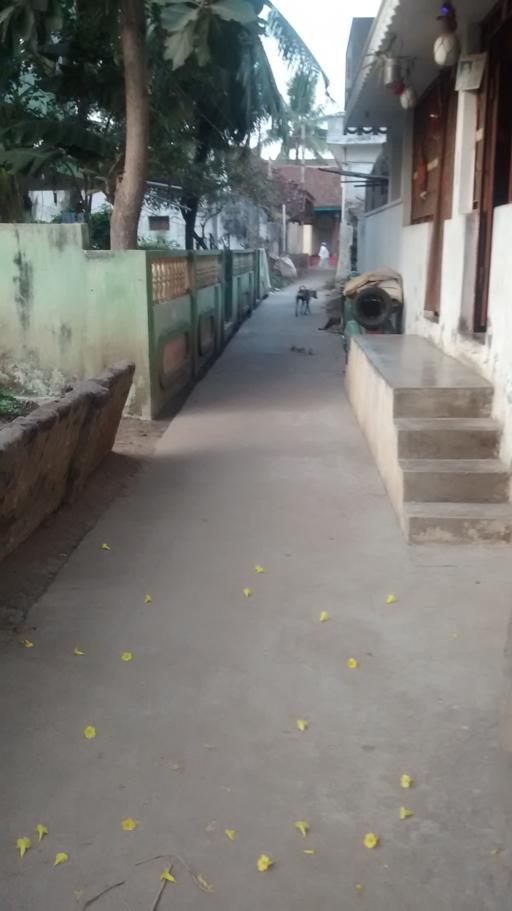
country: IN
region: Andhra Pradesh
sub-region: West Godavari
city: Akividu
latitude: 16.5371
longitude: 81.4110
